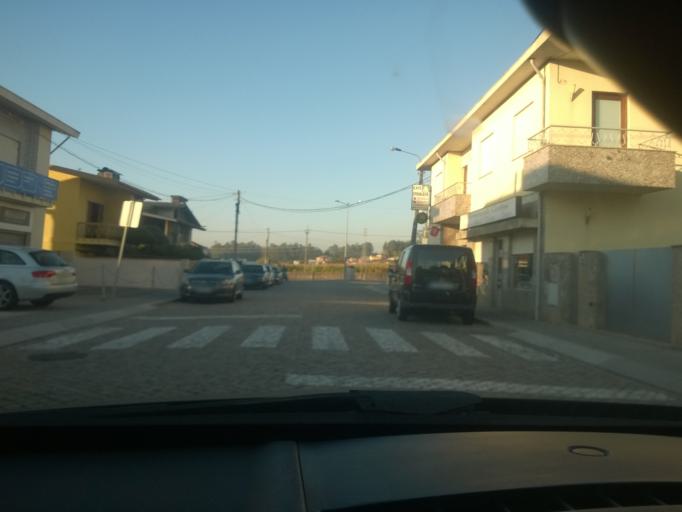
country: PT
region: Porto
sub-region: Maia
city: Anta
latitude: 41.2650
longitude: -8.6326
